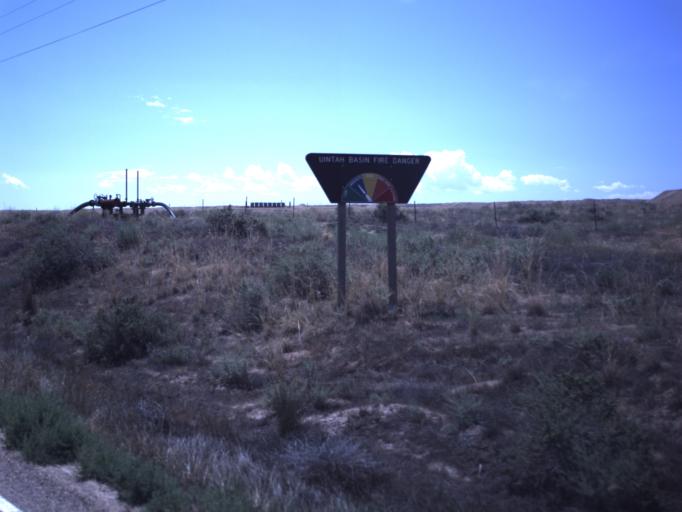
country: US
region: Utah
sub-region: Uintah County
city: Naples
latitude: 40.1364
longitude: -109.6639
